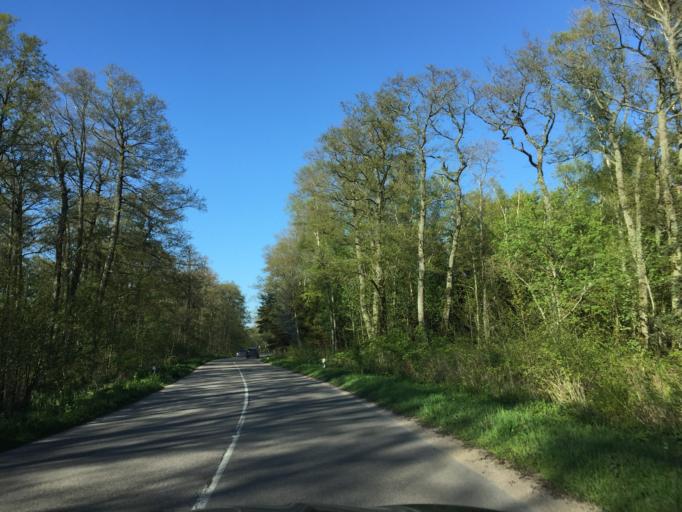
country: LT
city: Nida
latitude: 55.1952
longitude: 20.8642
